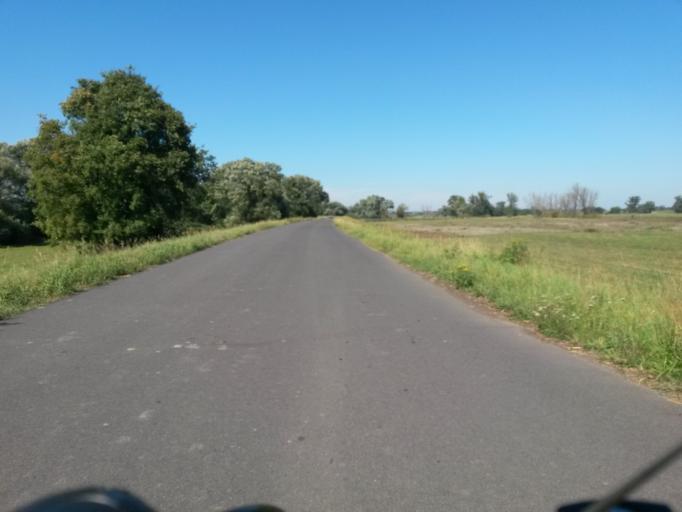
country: DE
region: Brandenburg
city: Schoneberg
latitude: 52.9258
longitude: 14.1279
